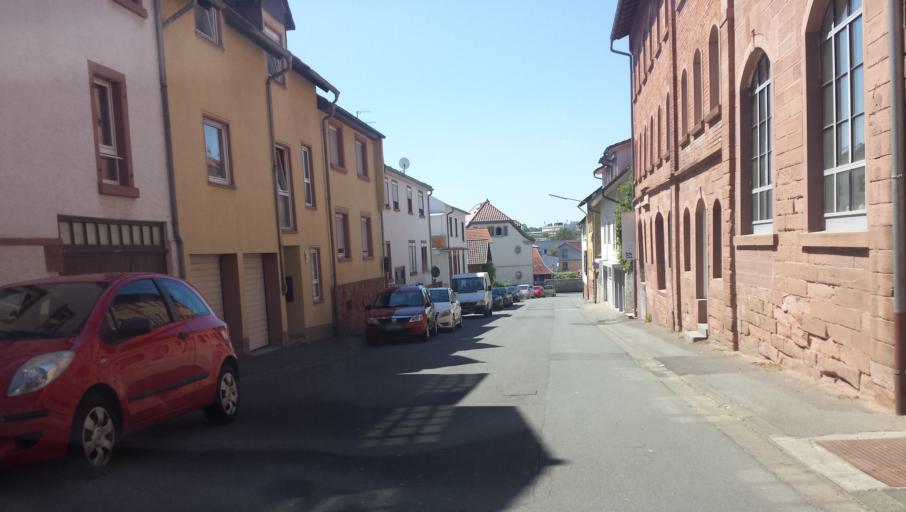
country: DE
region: Hesse
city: Gross-Umstadt
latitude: 49.8658
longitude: 8.9334
